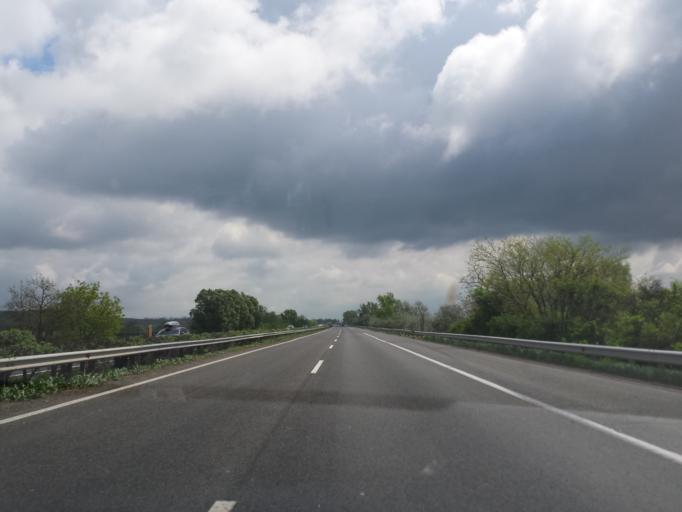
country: HU
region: Komarom-Esztergom
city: Mocsa
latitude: 47.6523
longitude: 18.1976
